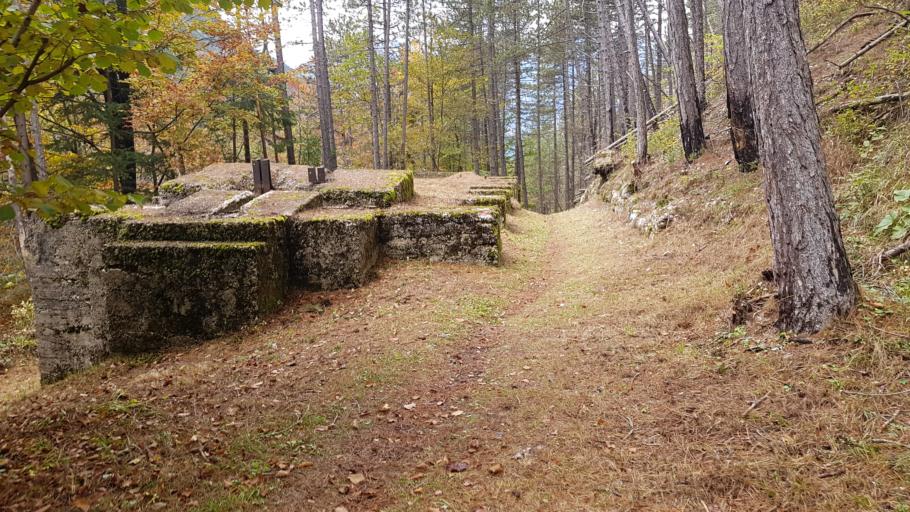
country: IT
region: Friuli Venezia Giulia
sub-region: Provincia di Udine
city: Chiusaforte
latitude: 46.4088
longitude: 13.3475
